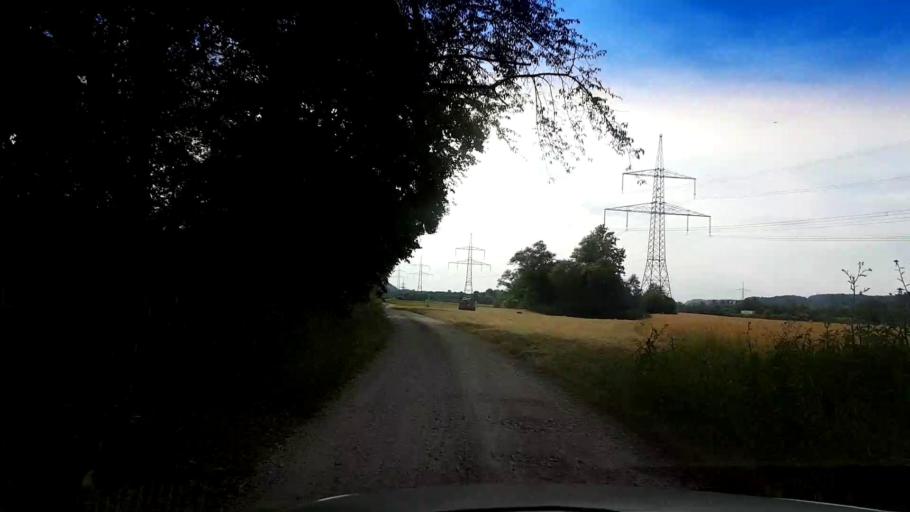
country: DE
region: Bavaria
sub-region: Regierungsbezirk Unterfranken
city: Ebelsbach
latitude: 49.9746
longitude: 10.6878
